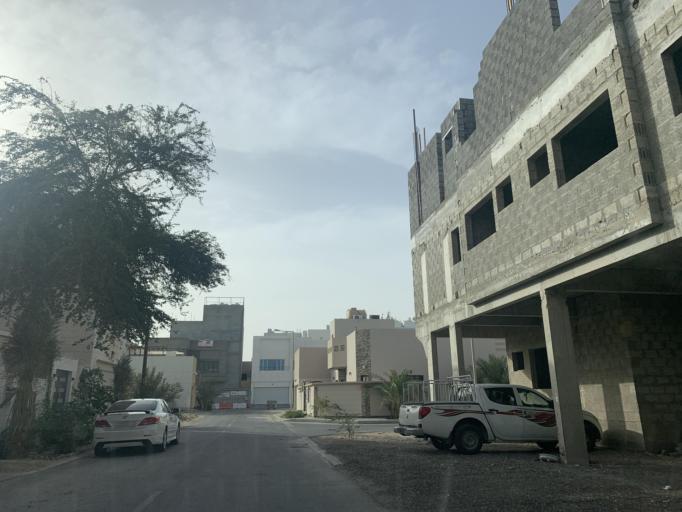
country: BH
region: Northern
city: Madinat `Isa
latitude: 26.1576
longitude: 50.5092
